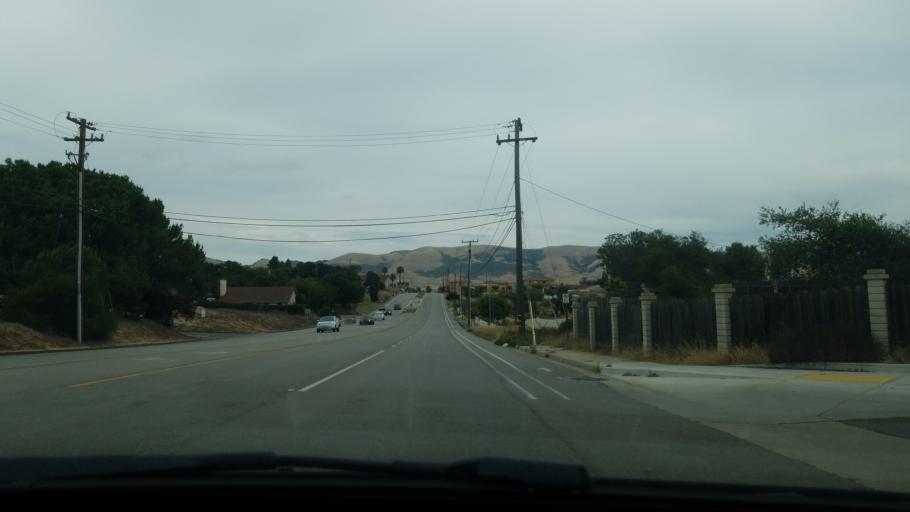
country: US
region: California
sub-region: San Luis Obispo County
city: Nipomo
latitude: 35.0317
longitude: -120.4937
